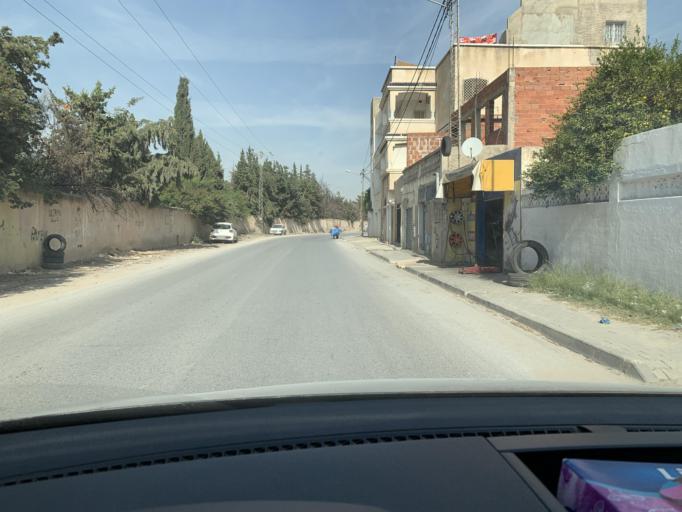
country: TN
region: Manouba
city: Manouba
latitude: 36.8155
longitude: 10.1171
